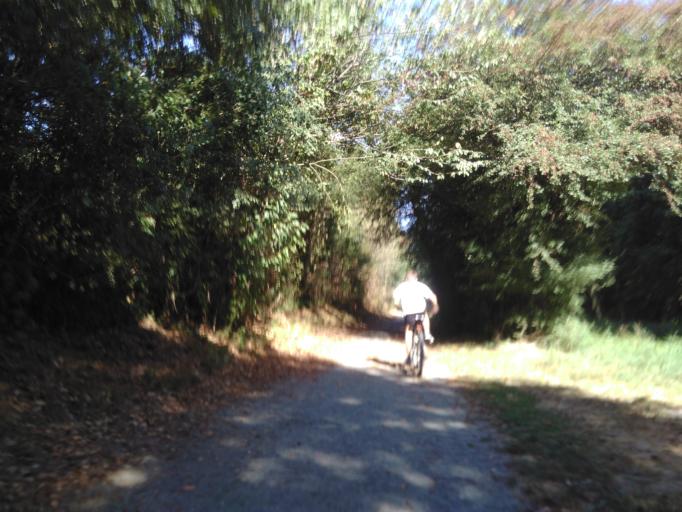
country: FR
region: Pays de la Loire
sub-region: Departement de la Vendee
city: La Chaize-le-Vicomte
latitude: 46.6645
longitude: -1.3012
